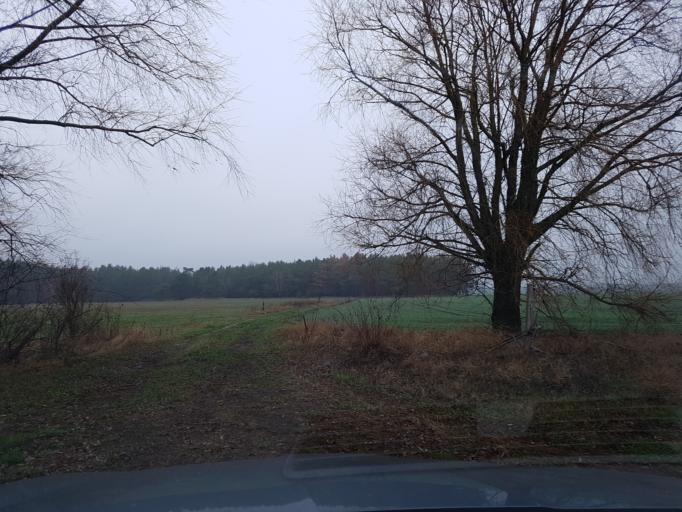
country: DE
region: Brandenburg
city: Schilda
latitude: 51.5964
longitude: 13.3955
